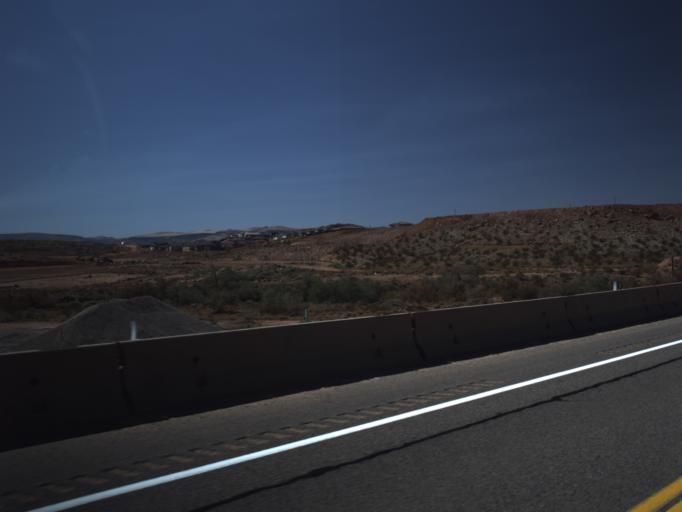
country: US
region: Utah
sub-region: Washington County
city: Washington
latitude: 37.0102
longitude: -113.5022
